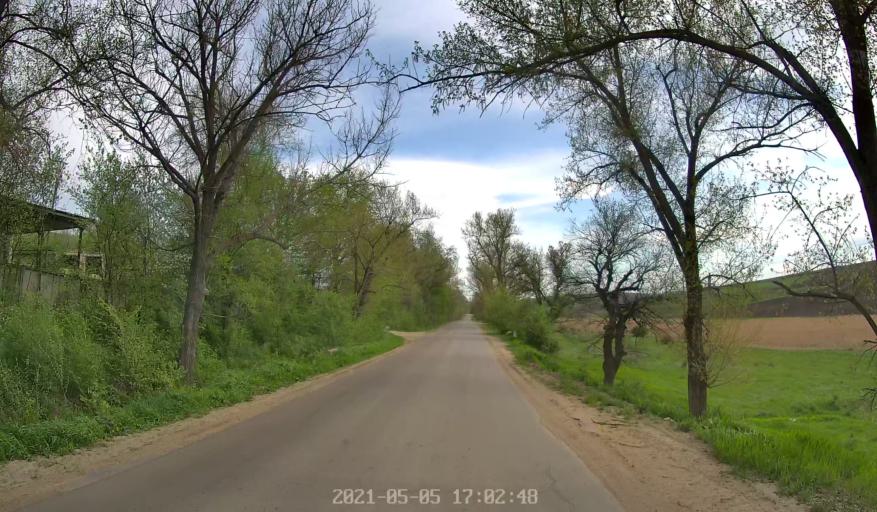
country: MD
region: Chisinau
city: Vadul lui Voda
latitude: 47.0571
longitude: 29.1322
